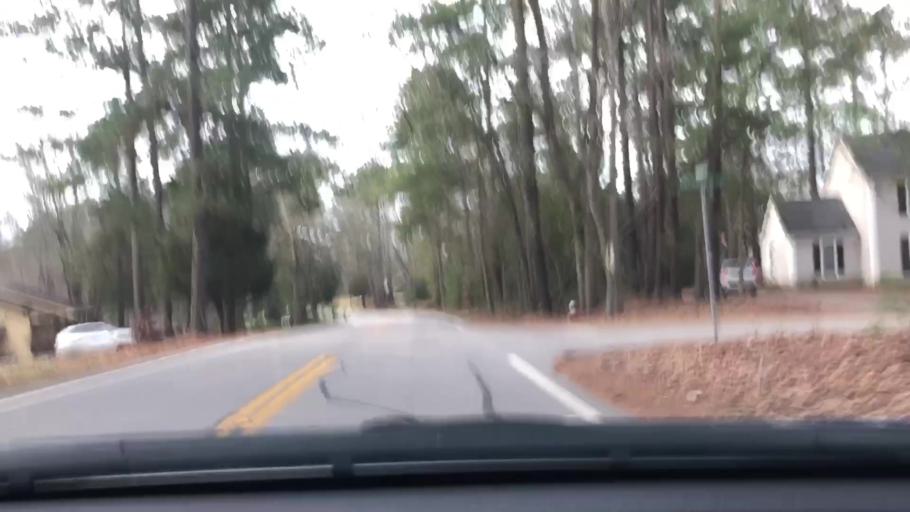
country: US
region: South Carolina
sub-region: Lexington County
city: Irmo
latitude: 34.0643
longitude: -81.1788
